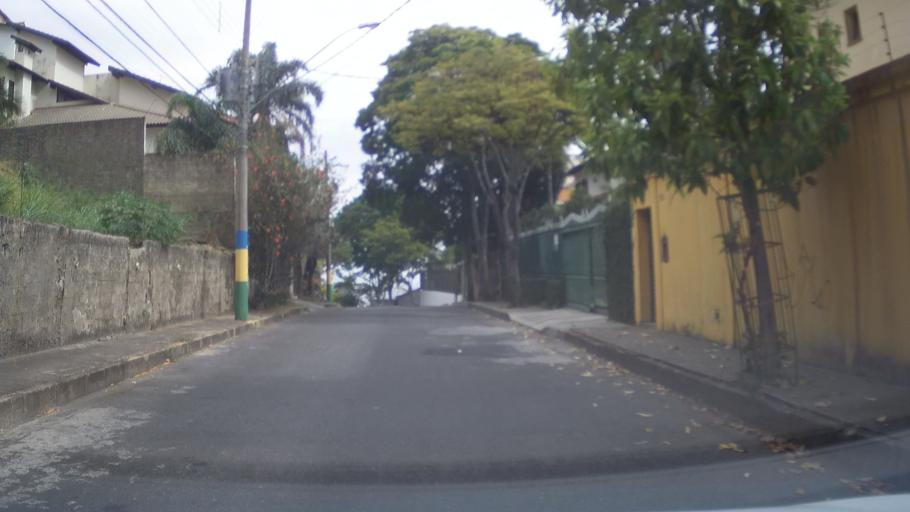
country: BR
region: Minas Gerais
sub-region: Belo Horizonte
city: Belo Horizonte
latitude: -19.9527
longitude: -43.9174
